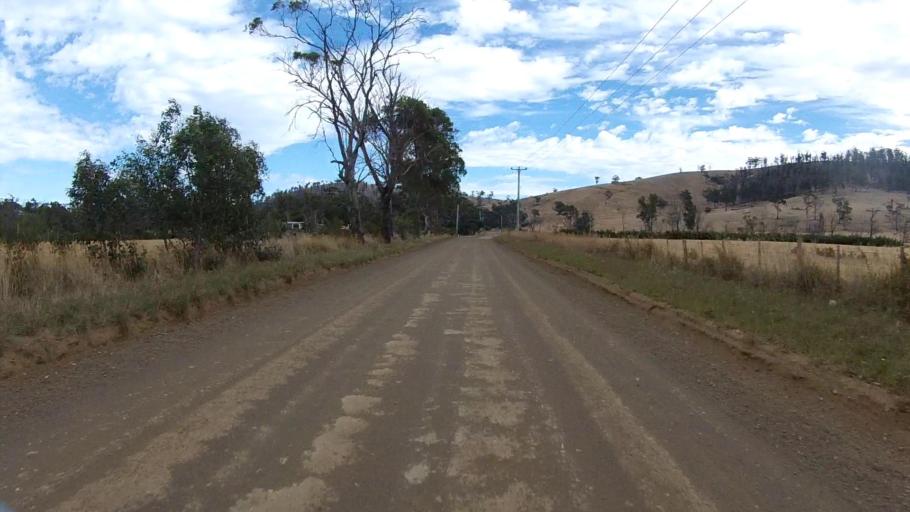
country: AU
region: Tasmania
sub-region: Sorell
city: Sorell
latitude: -42.8877
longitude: 147.7349
